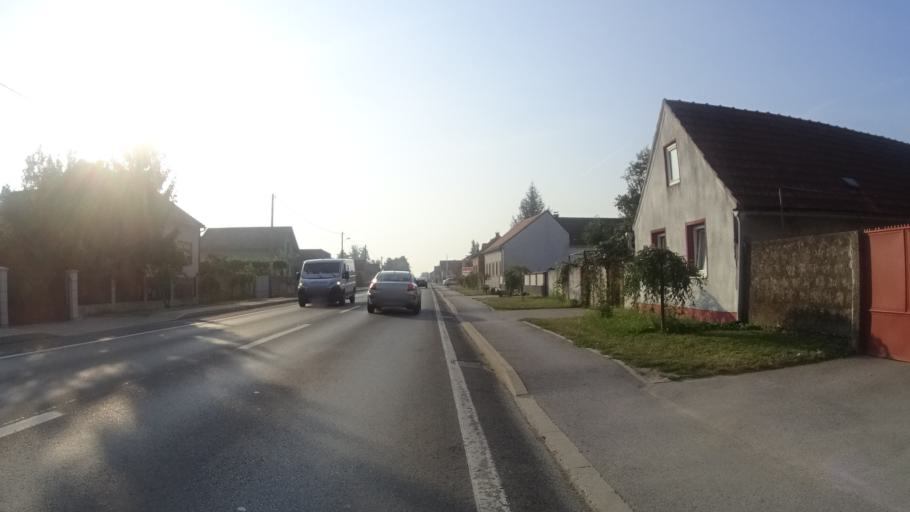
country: HR
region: Varazdinska
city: Sracinec
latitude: 46.3300
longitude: 16.2779
